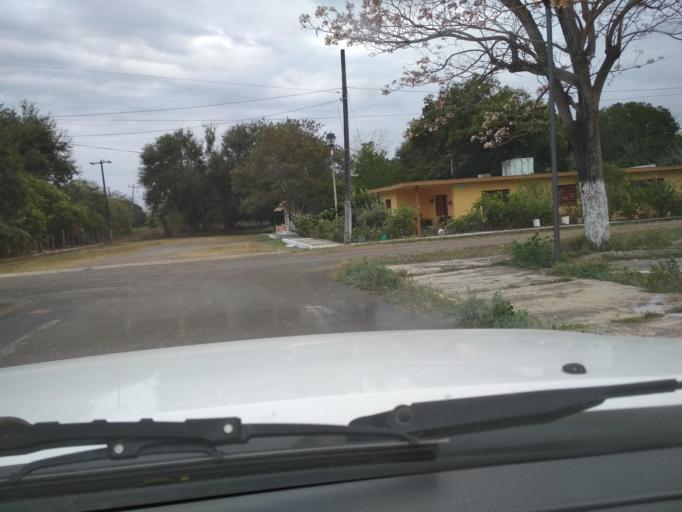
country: MX
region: Veracruz
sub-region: Veracruz
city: Delfino Victoria (Santa Fe)
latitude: 19.1595
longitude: -96.2951
